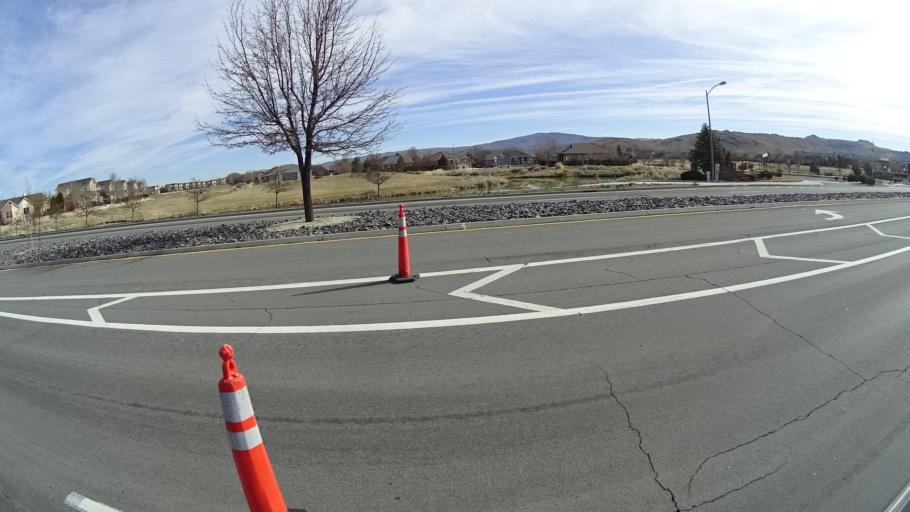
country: US
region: Nevada
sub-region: Washoe County
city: Sun Valley
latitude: 39.5910
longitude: -119.7307
